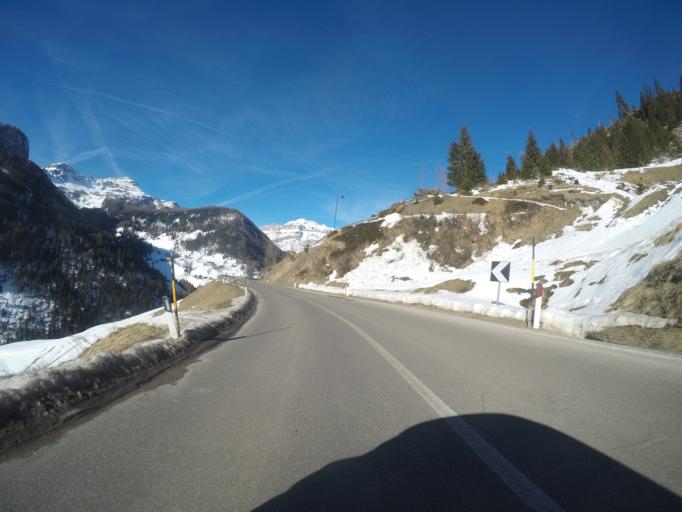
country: IT
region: Veneto
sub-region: Provincia di Belluno
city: Livinallongo del Col di Lana
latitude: 46.4877
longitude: 11.9433
